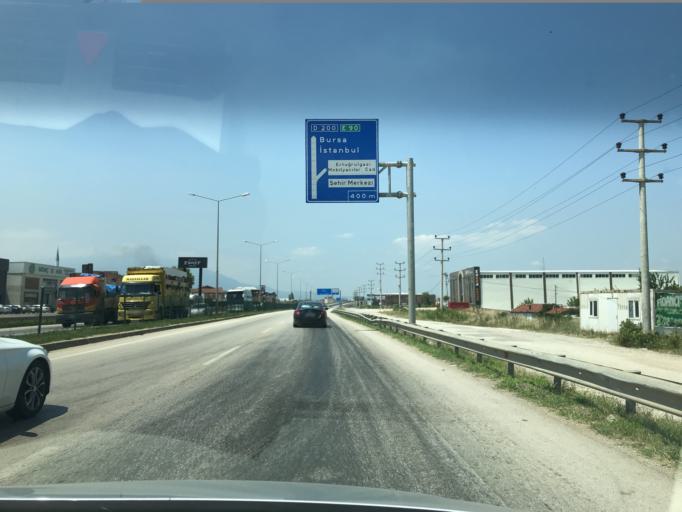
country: TR
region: Bursa
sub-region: Inegoel
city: Inegol
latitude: 40.0748
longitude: 29.5346
